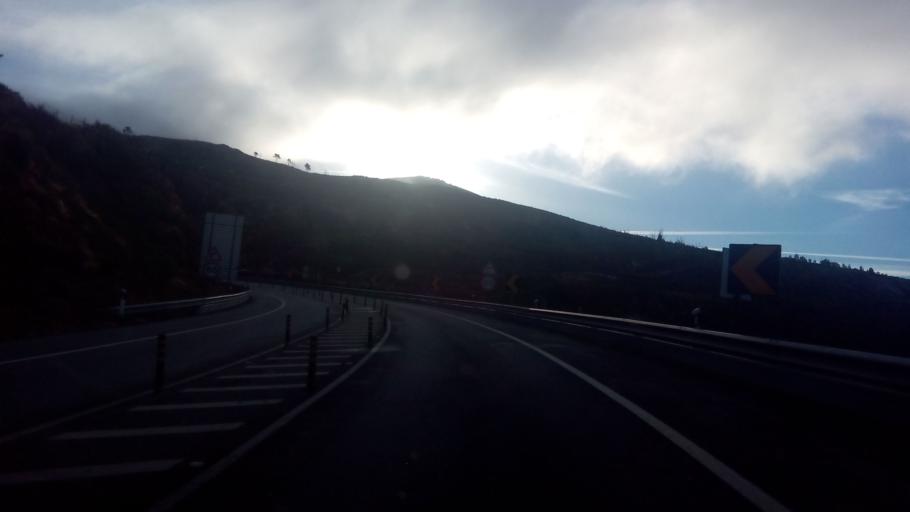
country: PT
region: Porto
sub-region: Amarante
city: Amarante
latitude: 41.2678
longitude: -7.9838
